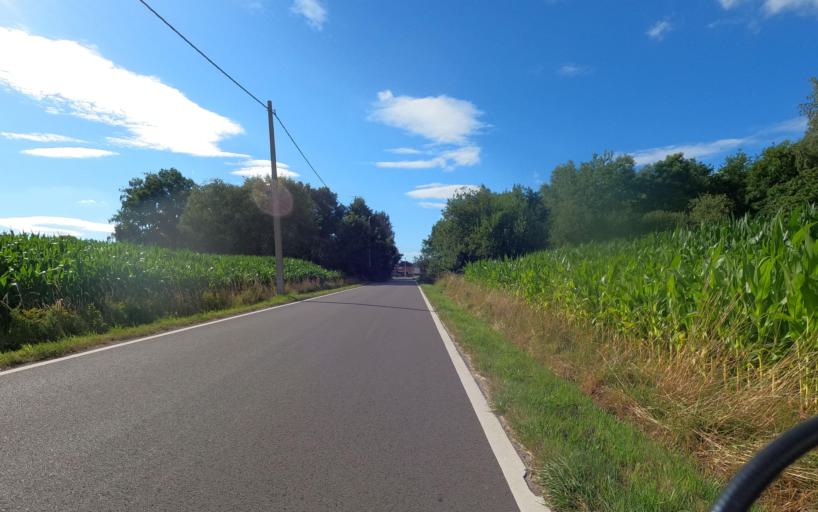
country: BE
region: Flanders
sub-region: Provincie Antwerpen
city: Heist-op-den-Berg
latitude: 51.0407
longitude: 4.7168
